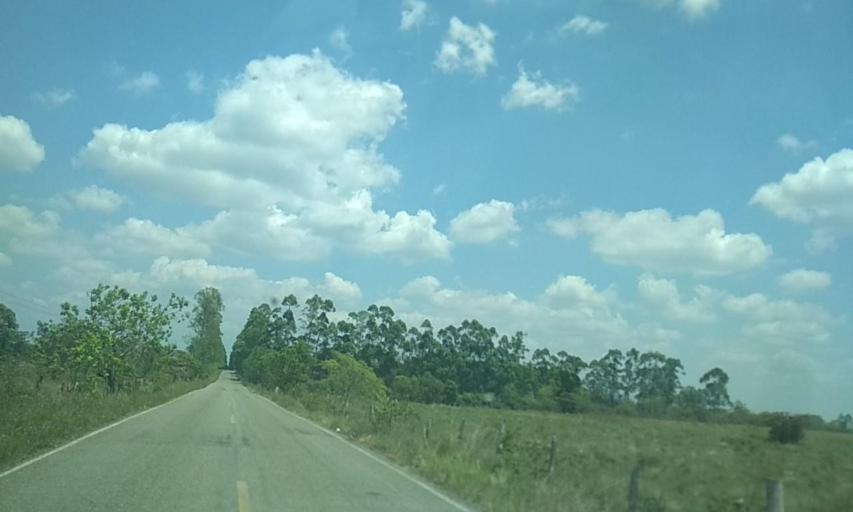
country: MX
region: Tabasco
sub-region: Huimanguillo
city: Francisco Rueda
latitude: 17.7665
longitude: -93.7967
